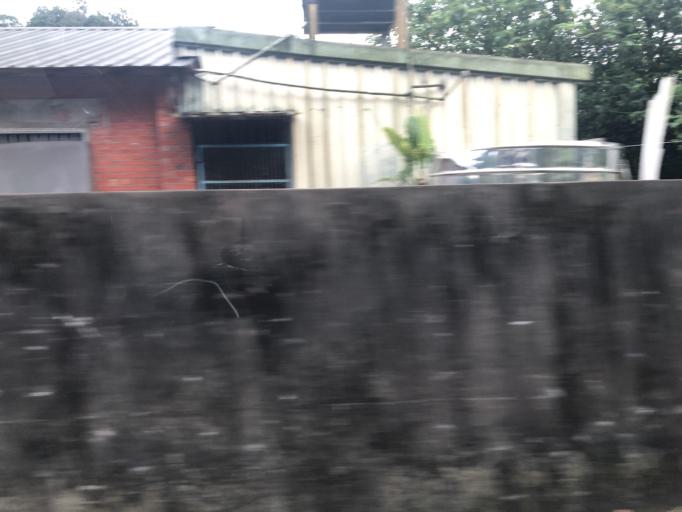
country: TW
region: Taiwan
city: Daxi
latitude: 24.9111
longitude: 121.3397
